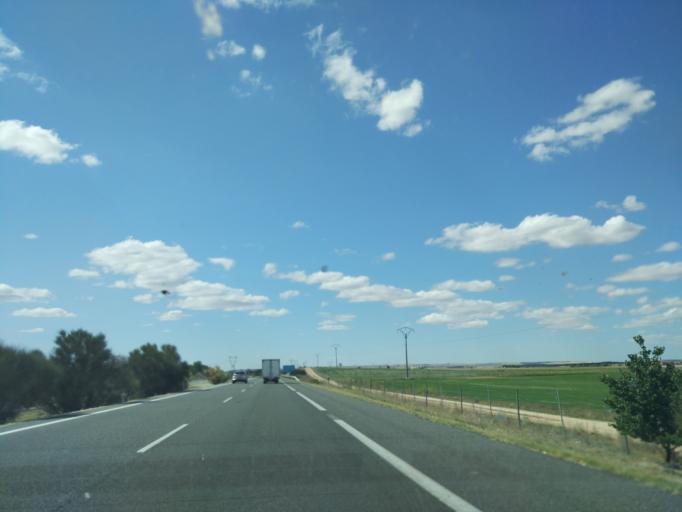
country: ES
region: Castille and Leon
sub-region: Provincia de Valladolid
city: San Vicente del Palacio
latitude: 41.2294
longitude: -4.8513
